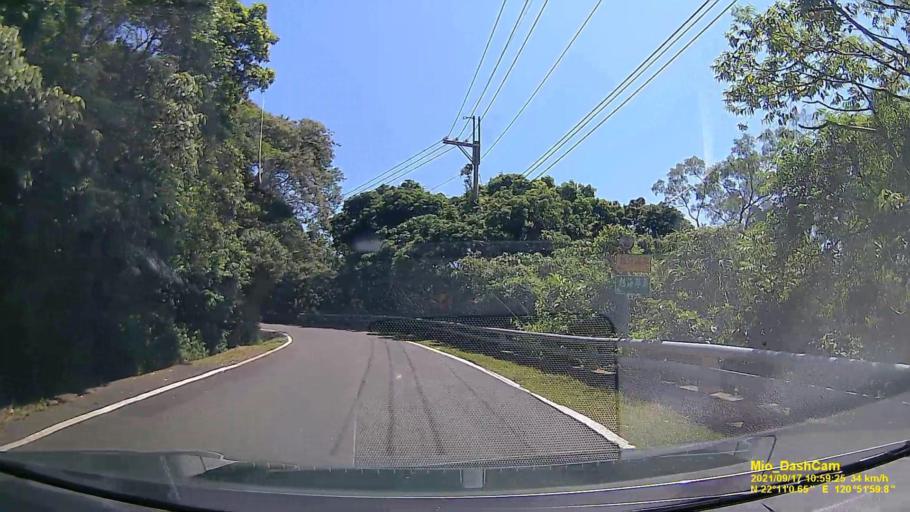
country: TW
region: Taiwan
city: Hengchun
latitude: 22.1835
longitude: 120.8666
